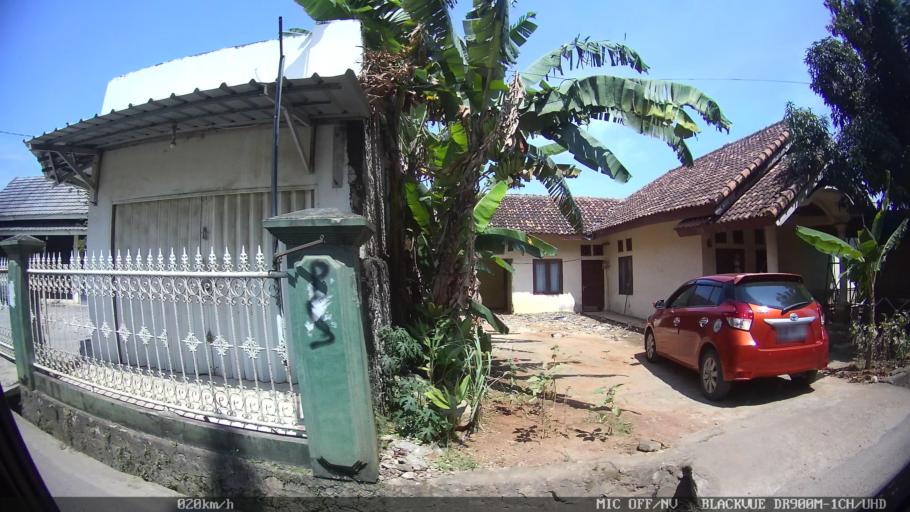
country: ID
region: Lampung
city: Kedaton
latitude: -5.3759
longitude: 105.2597
